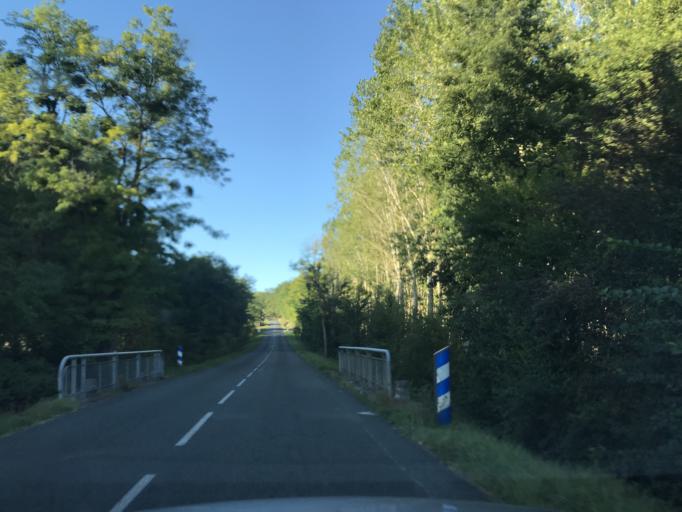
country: FR
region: Aquitaine
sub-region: Departement de la Gironde
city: Rauzan
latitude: 44.7736
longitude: -0.0608
